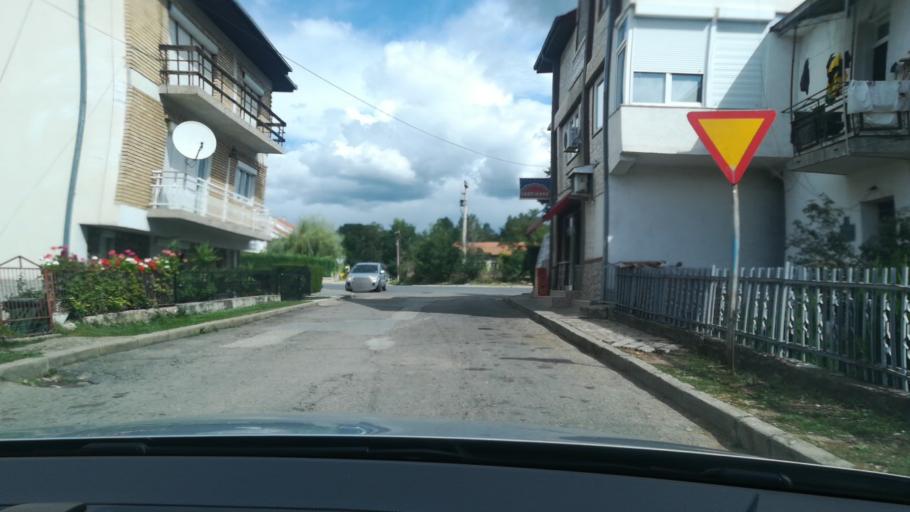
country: MK
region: Delcevo
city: Delcevo
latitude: 41.9636
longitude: 22.7797
